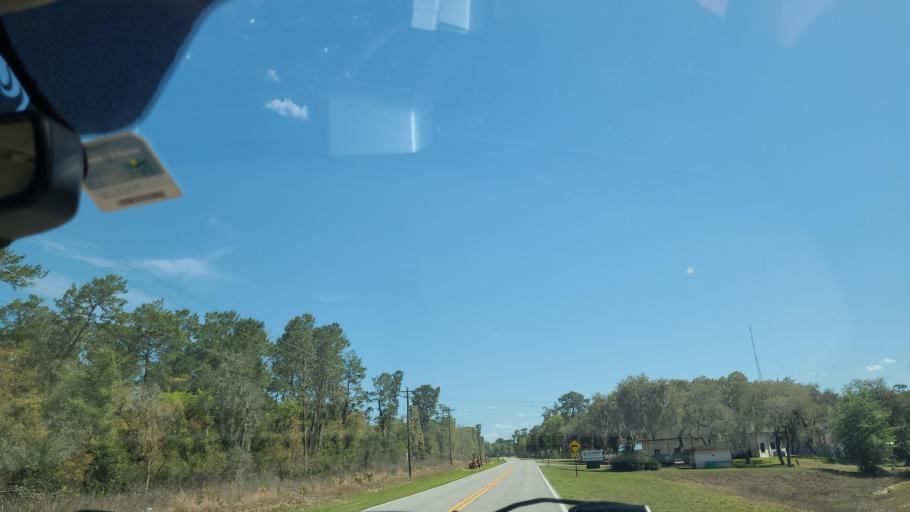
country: US
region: Florida
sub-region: Putnam County
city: Crescent City
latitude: 29.3657
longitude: -81.7402
